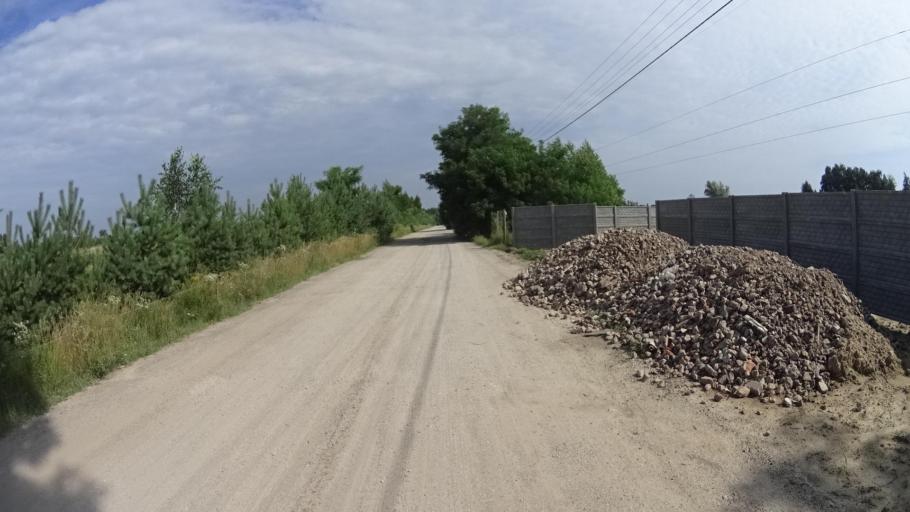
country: PL
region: Masovian Voivodeship
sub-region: Powiat piaseczynski
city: Tarczyn
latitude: 51.9725
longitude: 20.8539
